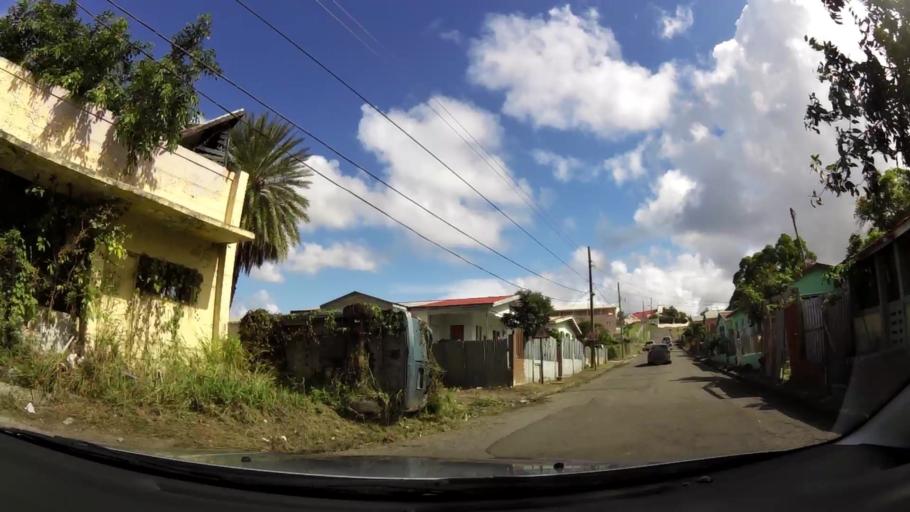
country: AG
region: Saint John
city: Saint John's
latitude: 17.1134
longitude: -61.8367
